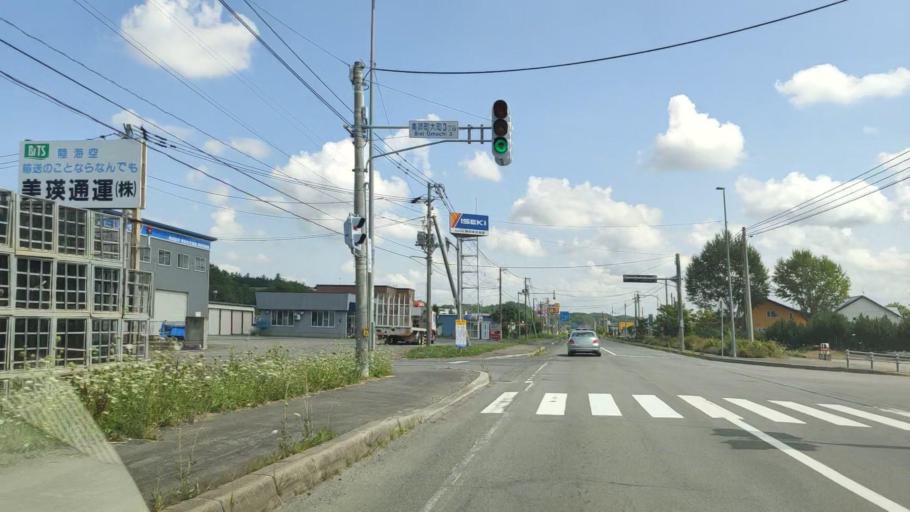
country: JP
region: Hokkaido
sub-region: Asahikawa-shi
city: Asahikawa
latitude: 43.5937
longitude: 142.4581
